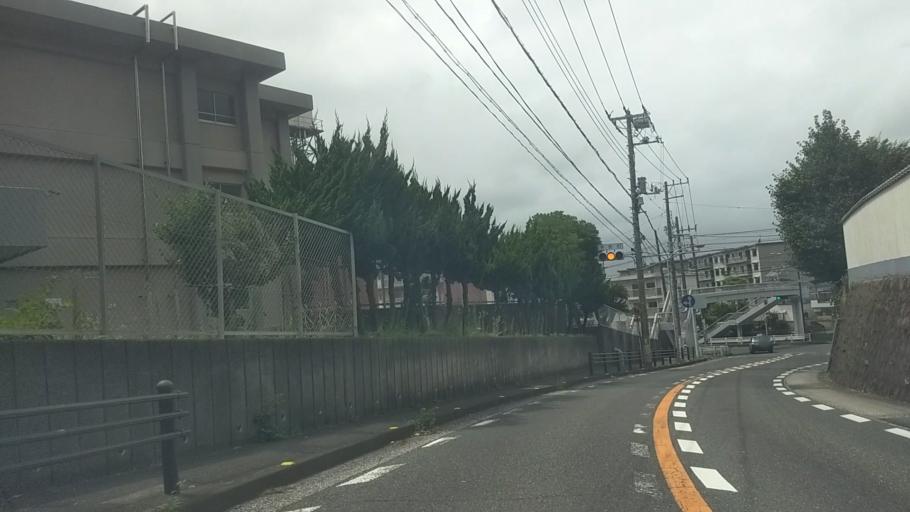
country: JP
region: Kanagawa
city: Yokosuka
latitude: 35.2601
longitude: 139.7158
